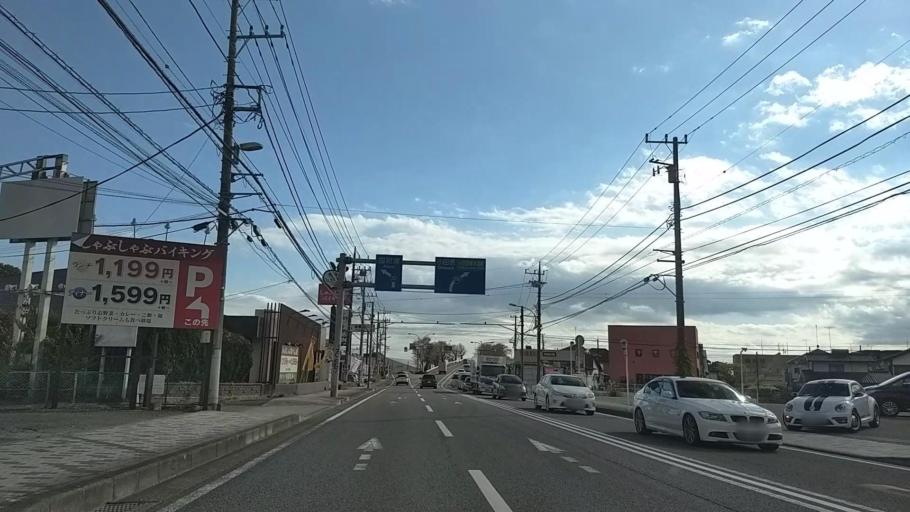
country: JP
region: Kanagawa
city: Odawara
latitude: 35.3295
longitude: 139.1572
